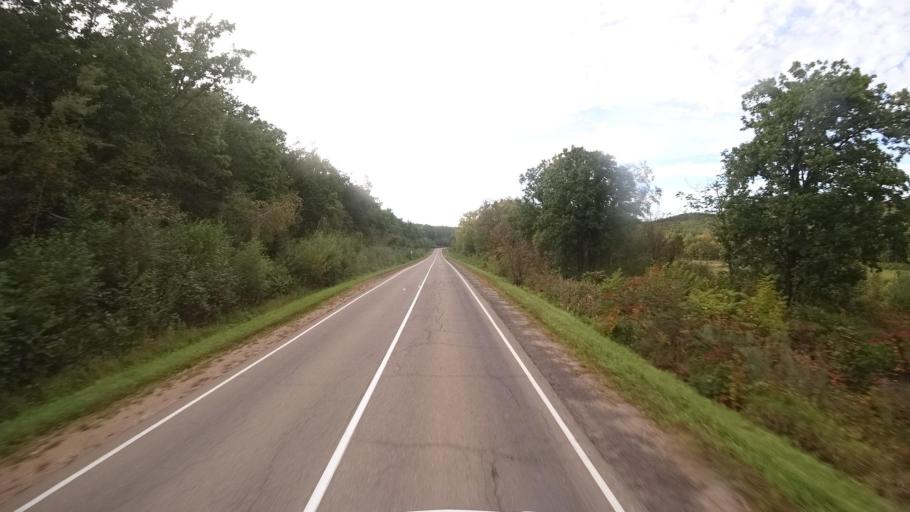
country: RU
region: Primorskiy
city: Yakovlevka
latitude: 44.4041
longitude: 133.4620
